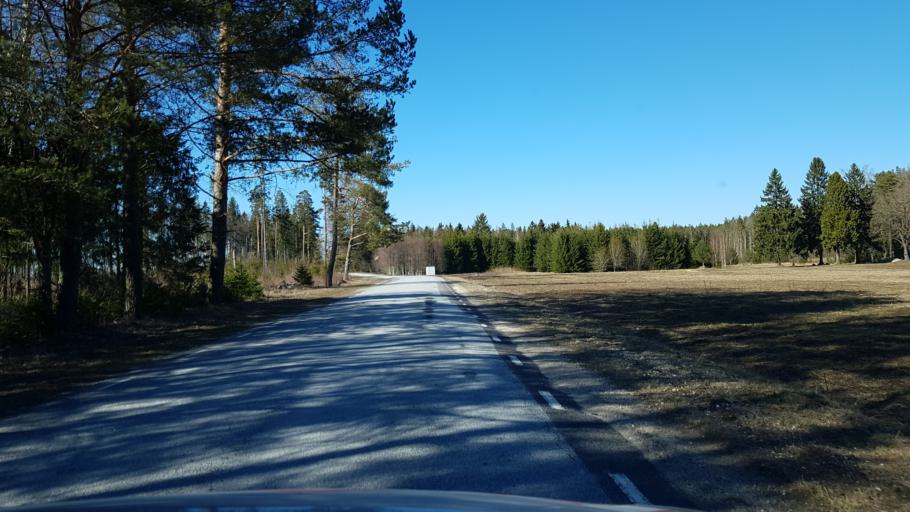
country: EE
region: Laeaene-Virumaa
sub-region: Viru-Nigula vald
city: Kunda
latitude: 59.3769
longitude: 26.5781
